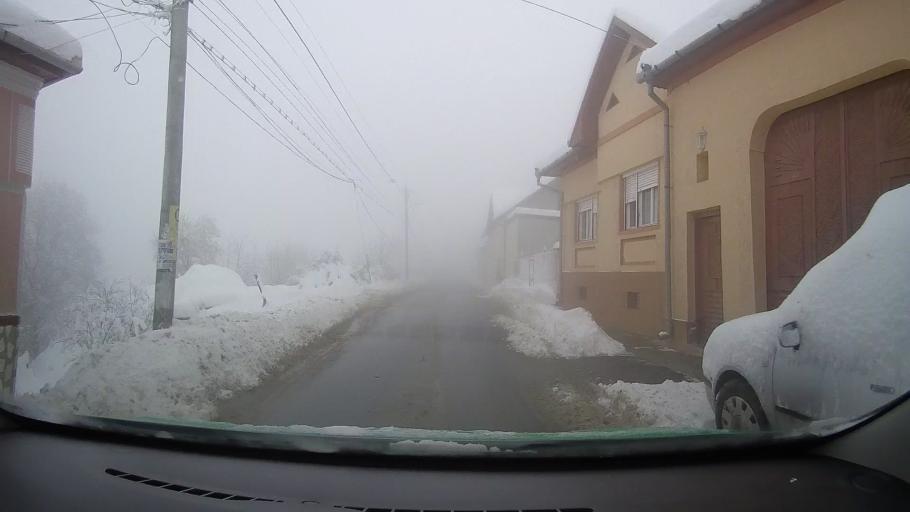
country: RO
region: Sibiu
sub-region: Comuna Poiana Sibiului
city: Poiana Sibiului
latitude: 45.8094
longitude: 23.7403
